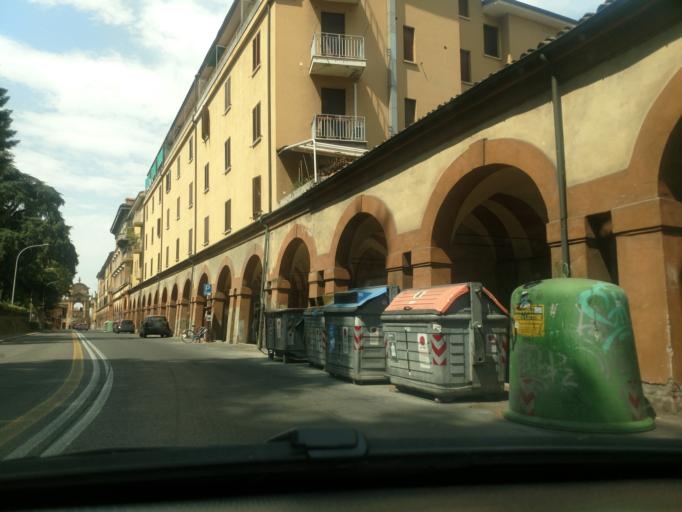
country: IT
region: Emilia-Romagna
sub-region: Provincia di Bologna
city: Bologna
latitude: 44.4900
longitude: 11.3142
